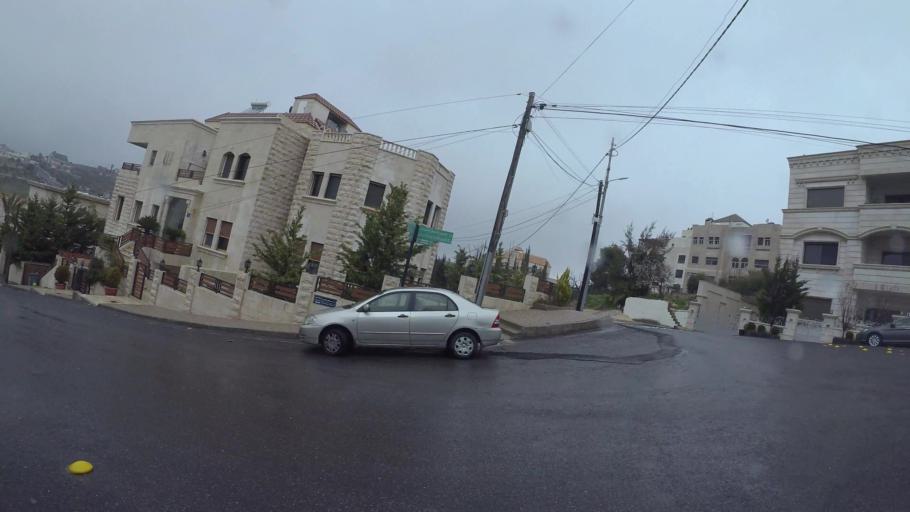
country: JO
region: Amman
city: Wadi as Sir
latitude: 31.9983
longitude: 35.8184
